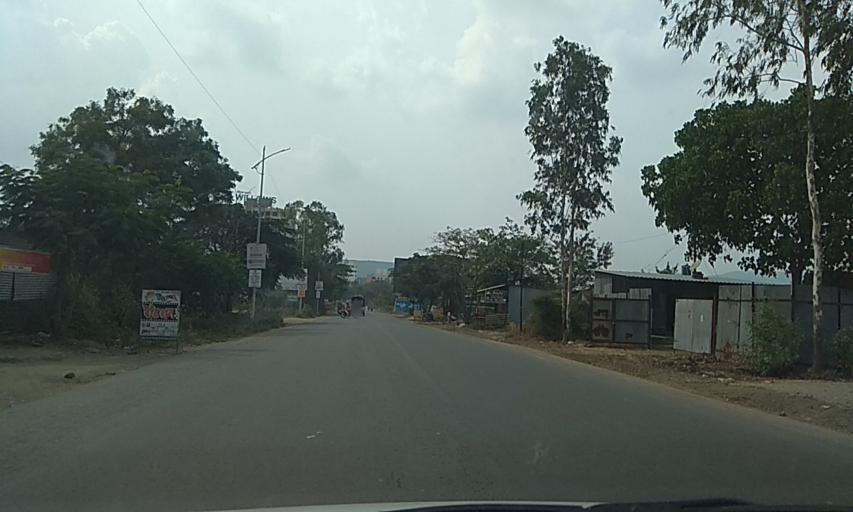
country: IN
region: Maharashtra
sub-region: Pune Division
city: Pimpri
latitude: 18.5782
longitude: 73.7154
